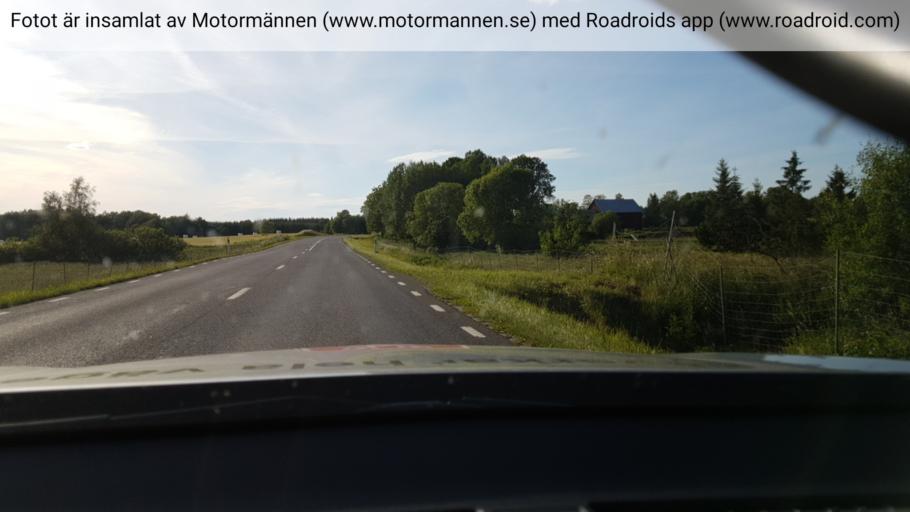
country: SE
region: Vaestra Goetaland
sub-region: Falkopings Kommun
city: Falkoeping
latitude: 58.0637
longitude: 13.5332
